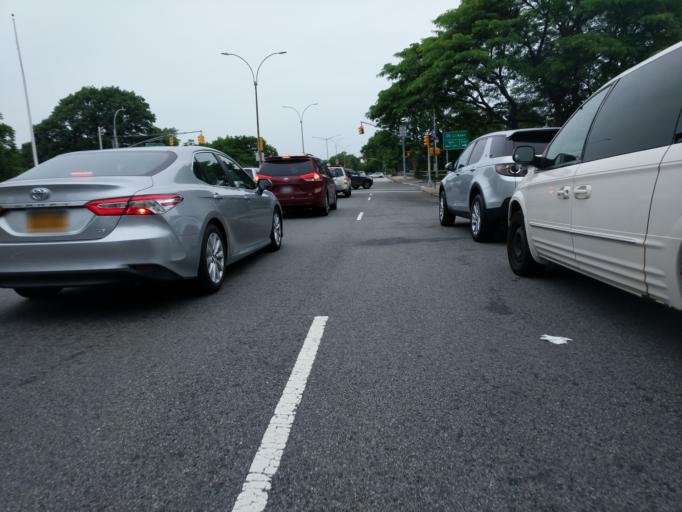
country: US
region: New York
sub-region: Nassau County
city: Bellerose Terrace
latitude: 40.7426
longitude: -73.7753
